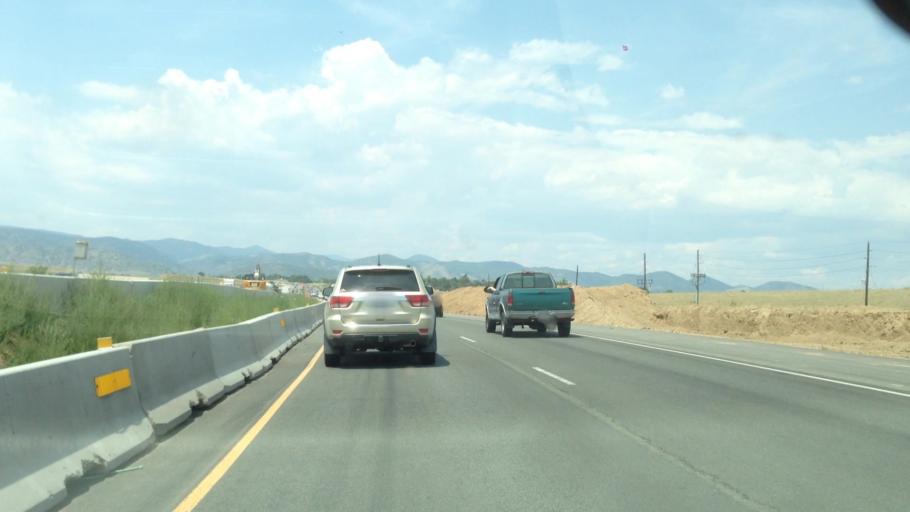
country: US
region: Colorado
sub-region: Jefferson County
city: Columbine
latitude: 39.5679
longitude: -105.0469
